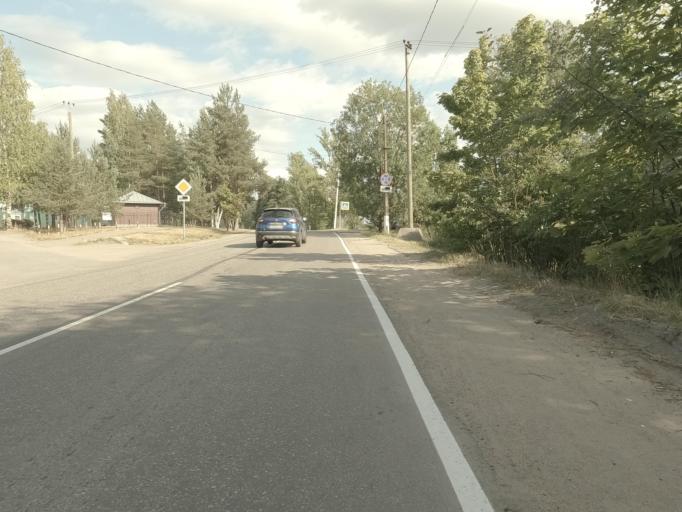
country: RU
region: Leningrad
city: Kamennogorsk
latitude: 60.9478
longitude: 29.1332
